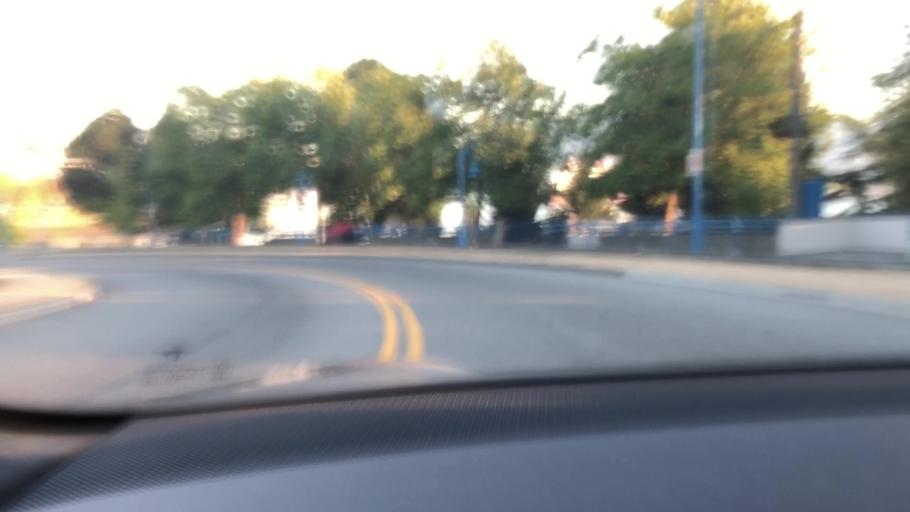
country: CA
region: British Columbia
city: West End
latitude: 49.2851
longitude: -123.0993
